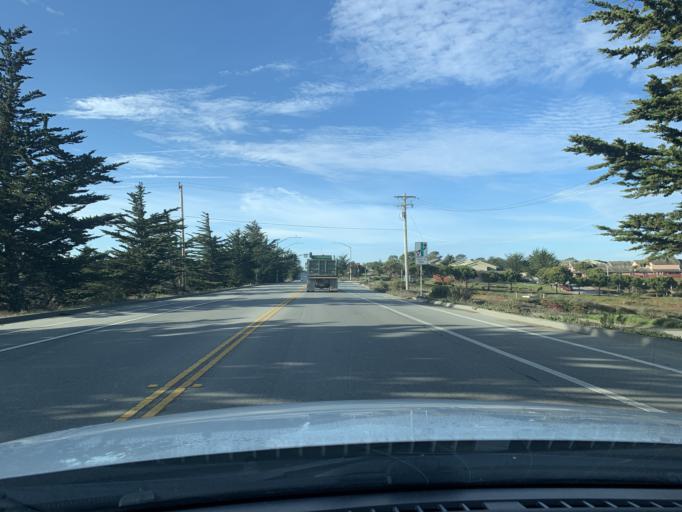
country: US
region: California
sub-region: Monterey County
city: Marina
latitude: 36.6690
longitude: -121.7695
